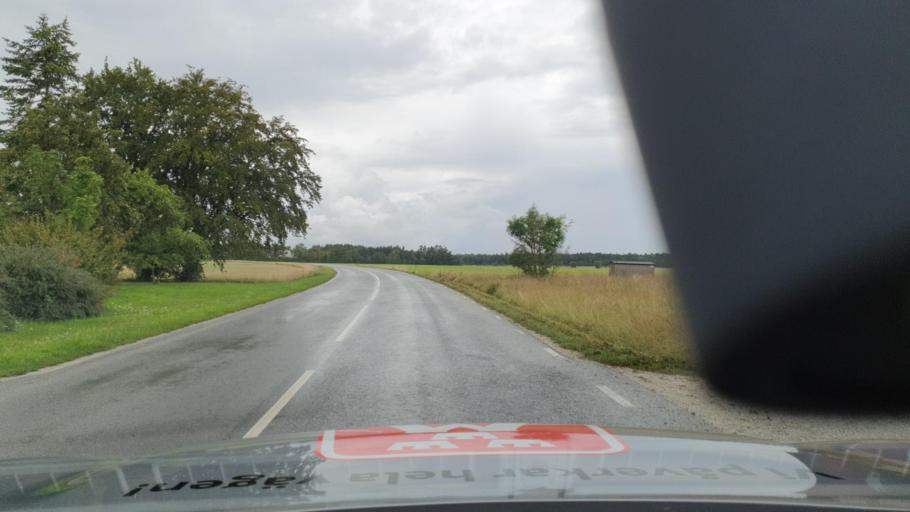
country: SE
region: Gotland
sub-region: Gotland
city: Visby
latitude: 57.5060
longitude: 18.4116
